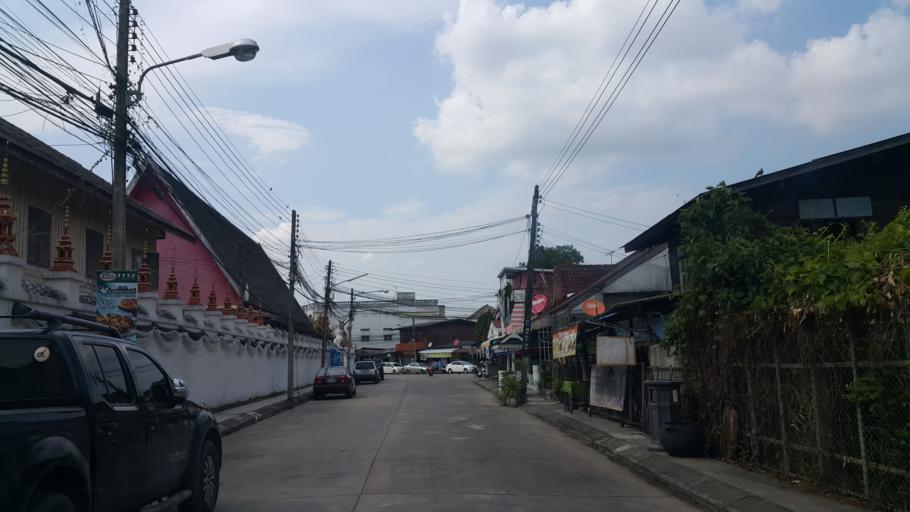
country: TH
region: Chiang Rai
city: Chiang Rai
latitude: 19.9028
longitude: 99.8316
